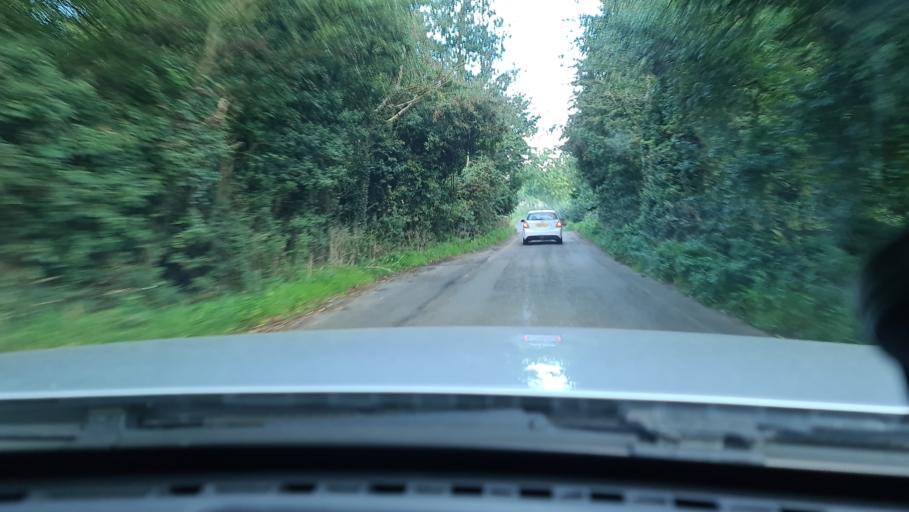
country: GB
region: England
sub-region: Oxfordshire
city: Hanwell
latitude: 52.0950
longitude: -1.3541
